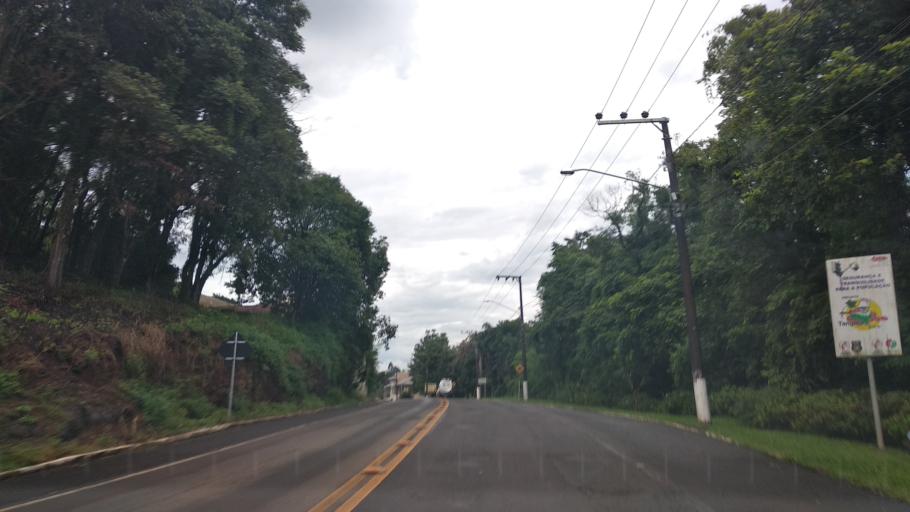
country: BR
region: Santa Catarina
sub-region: Videira
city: Videira
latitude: -27.0967
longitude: -51.2485
